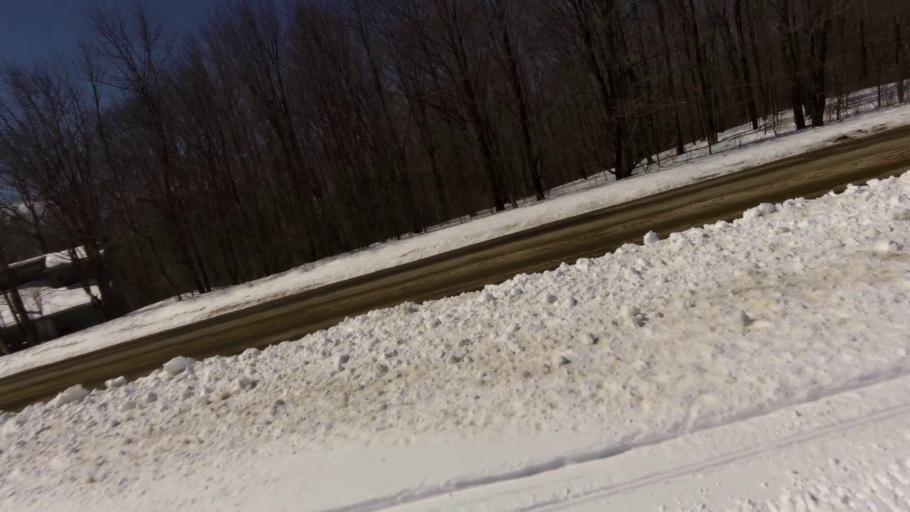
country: US
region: New York
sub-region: Allegany County
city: Houghton
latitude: 42.3500
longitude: -78.2602
